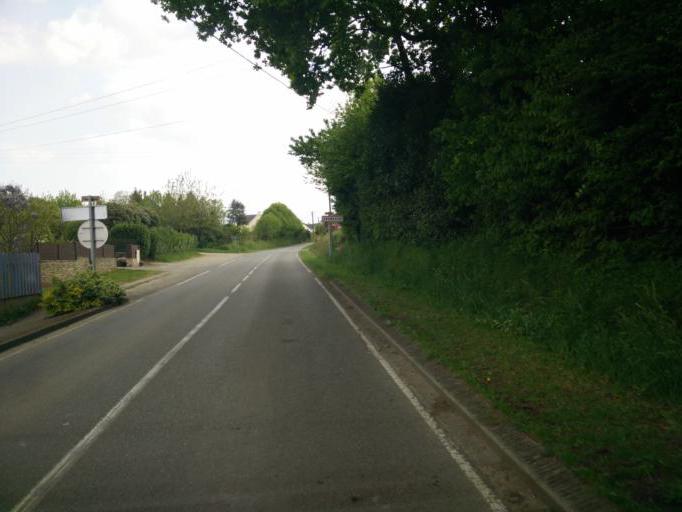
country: FR
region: Brittany
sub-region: Departement du Finistere
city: Tremeven
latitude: 47.9096
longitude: -3.5193
